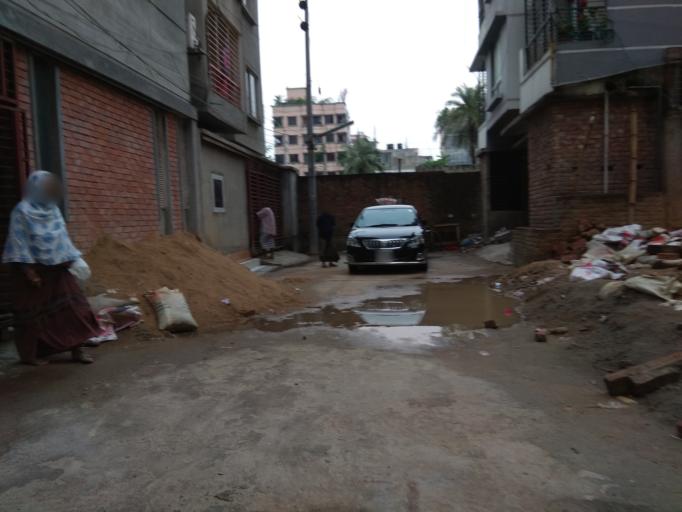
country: BD
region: Dhaka
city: Tungi
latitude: 23.8234
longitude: 90.3717
